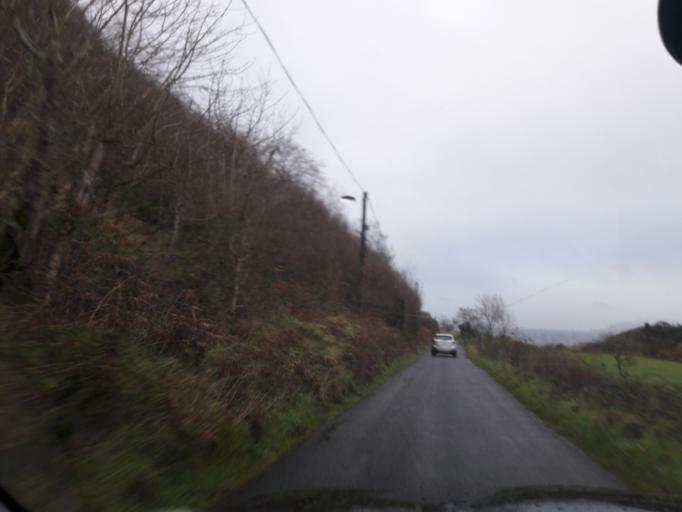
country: IE
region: Ulster
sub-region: County Donegal
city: Ramelton
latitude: 55.2260
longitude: -7.6234
